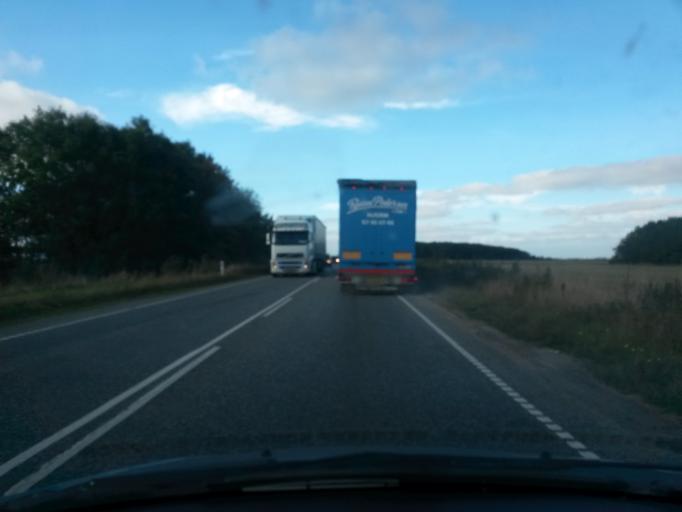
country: DK
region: Central Jutland
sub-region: Holstebro Kommune
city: Holstebro
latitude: 56.3351
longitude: 8.6482
